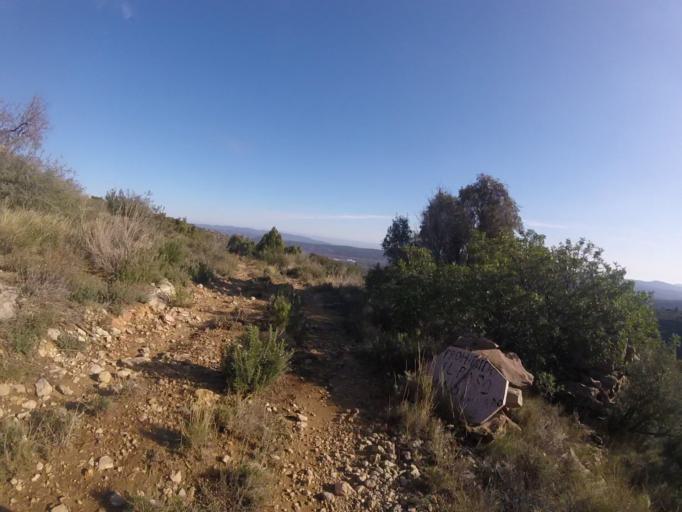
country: ES
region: Valencia
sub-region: Provincia de Castello
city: Sarratella
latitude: 40.2966
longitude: 0.0459
